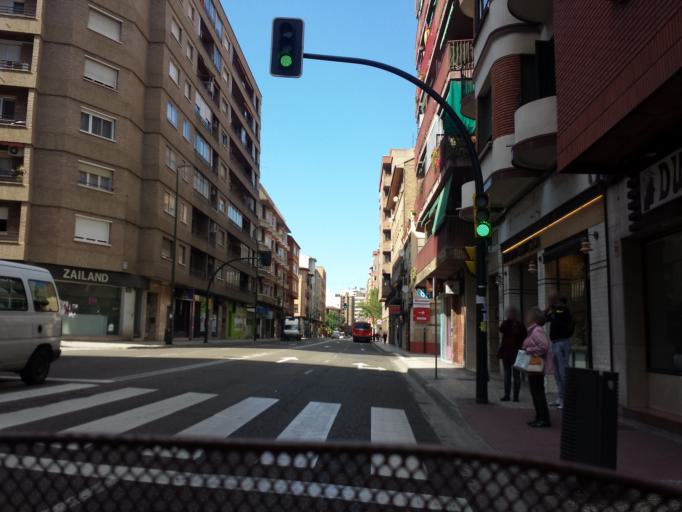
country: ES
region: Aragon
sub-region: Provincia de Zaragoza
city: Zaragoza
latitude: 41.6421
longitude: -0.8731
